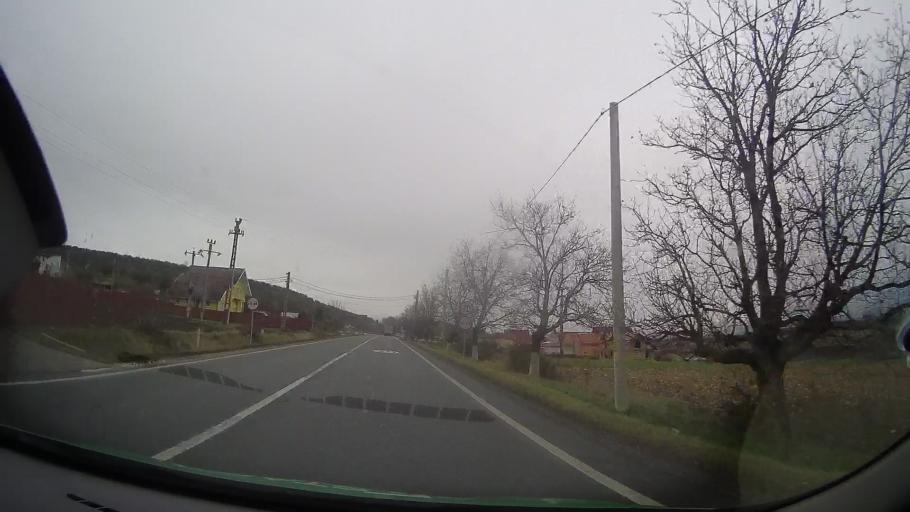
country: RO
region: Mures
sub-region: Comuna Breaza
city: Breaza
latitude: 46.7712
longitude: 24.6574
